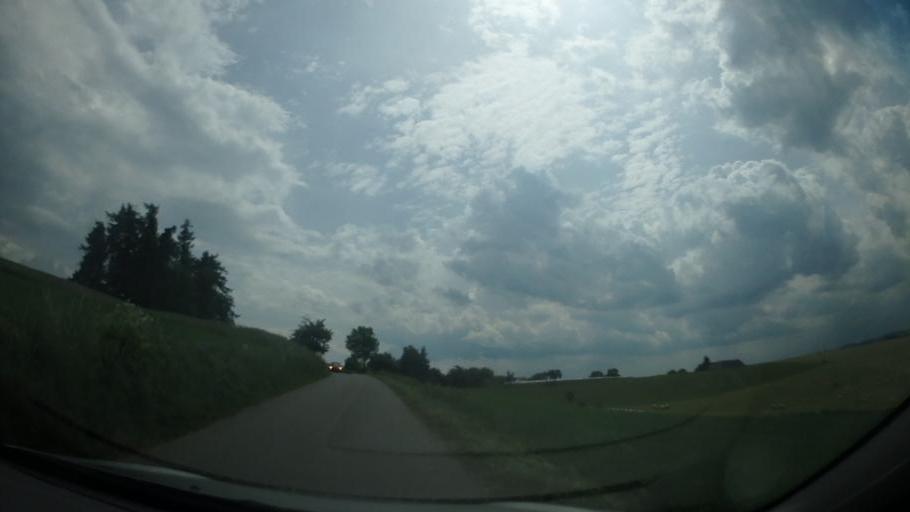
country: CZ
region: Vysocina
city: Bystrice nad Pernstejnem
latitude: 49.4696
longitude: 16.2306
